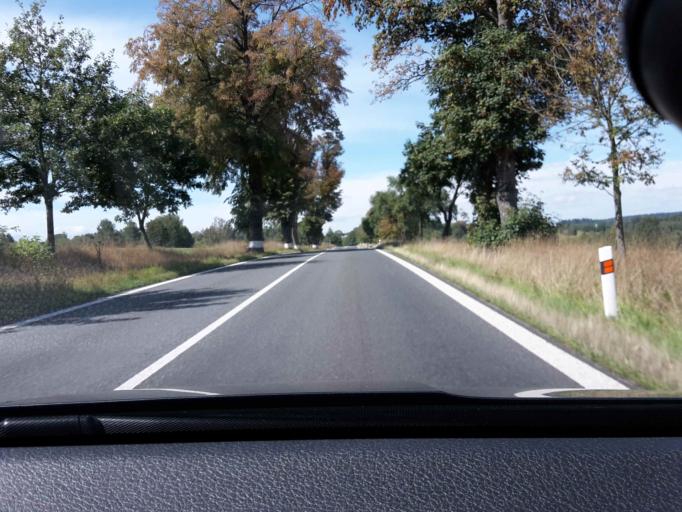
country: CZ
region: Jihocesky
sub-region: Okres Jindrichuv Hradec
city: Jindrichuv Hradec
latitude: 49.1576
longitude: 14.9676
